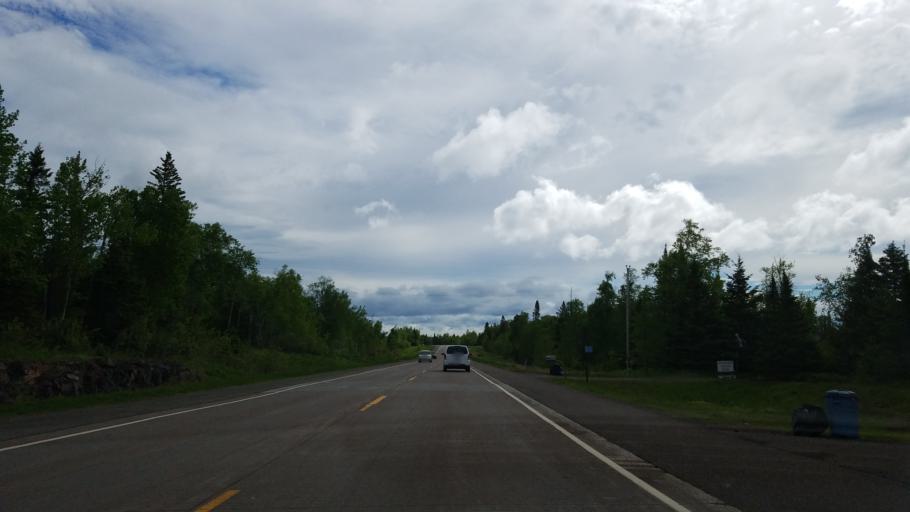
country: US
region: Minnesota
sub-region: Lake County
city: Two Harbors
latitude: 47.1050
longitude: -91.5303
